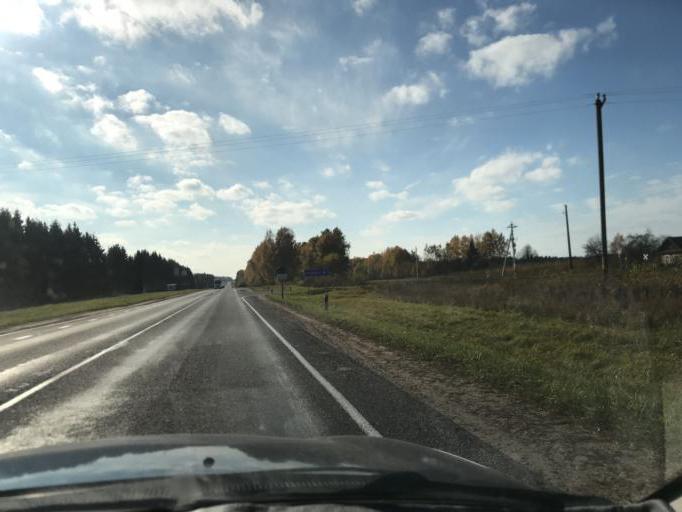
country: BY
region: Grodnenskaya
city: Voranava
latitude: 54.2089
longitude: 25.3507
